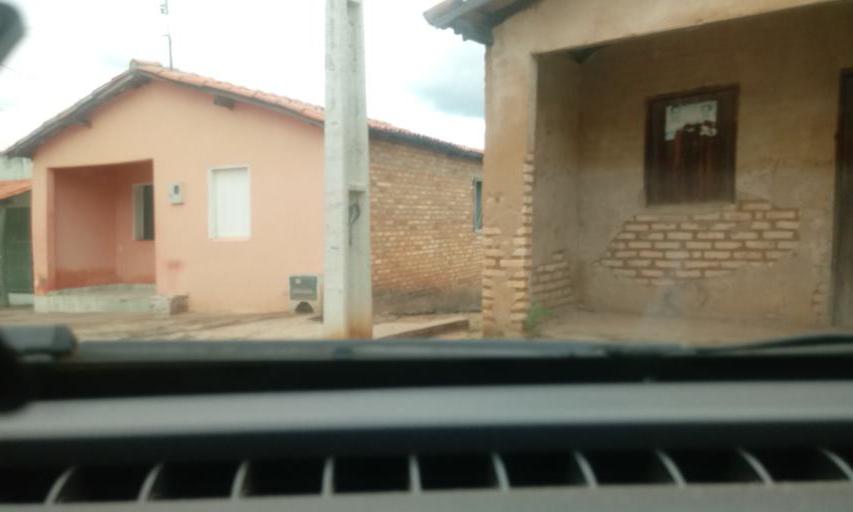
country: BR
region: Bahia
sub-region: Riacho De Santana
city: Riacho de Santana
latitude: -13.9126
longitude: -42.8478
